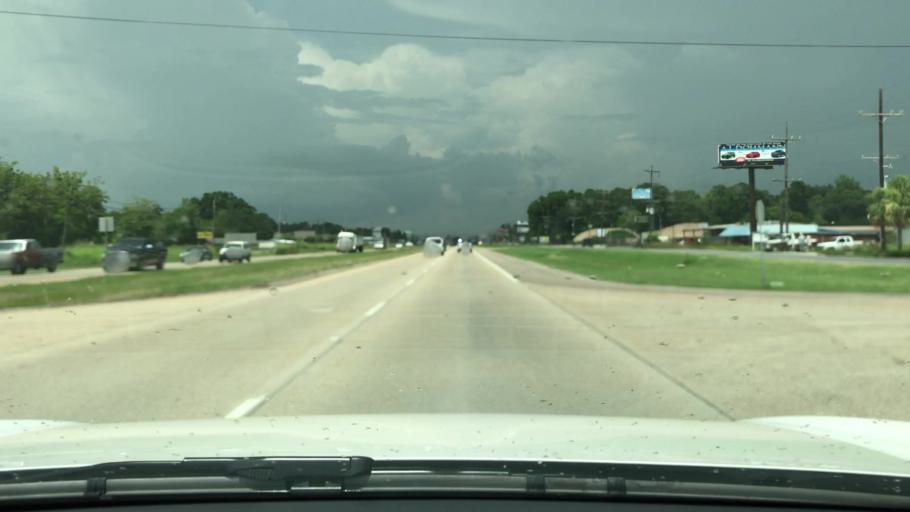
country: US
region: Louisiana
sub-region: West Baton Rouge Parish
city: Brusly
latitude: 30.4095
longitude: -91.2280
